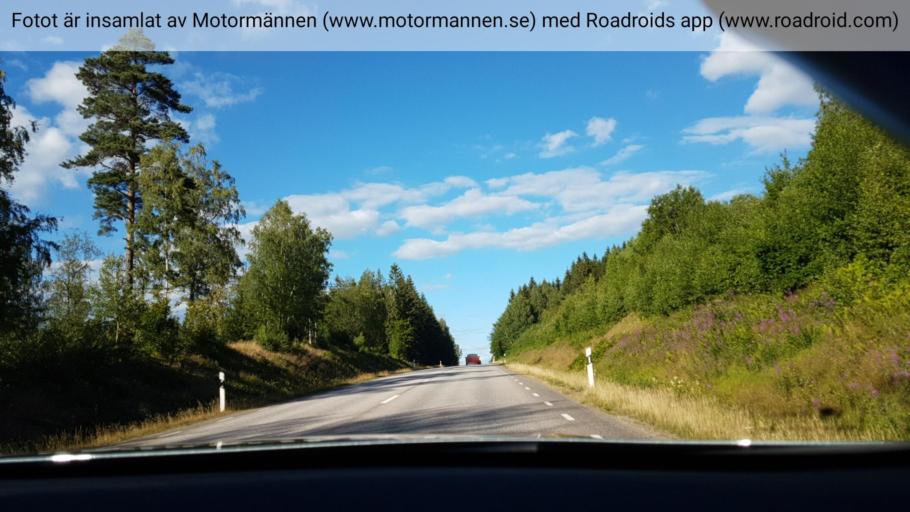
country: SE
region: Vaestra Goetaland
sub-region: Tibro Kommun
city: Tibro
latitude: 58.4570
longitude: 14.2732
